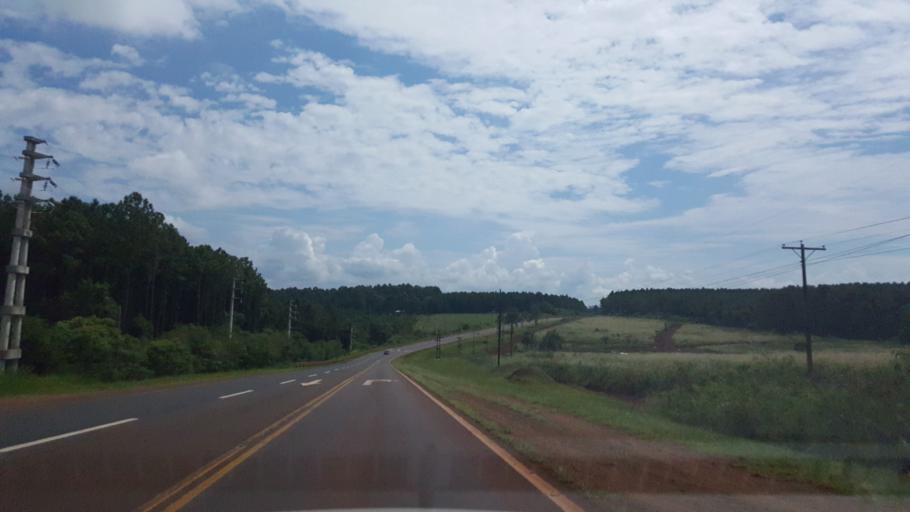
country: AR
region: Misiones
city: Capiovi
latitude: -26.9074
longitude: -55.0610
